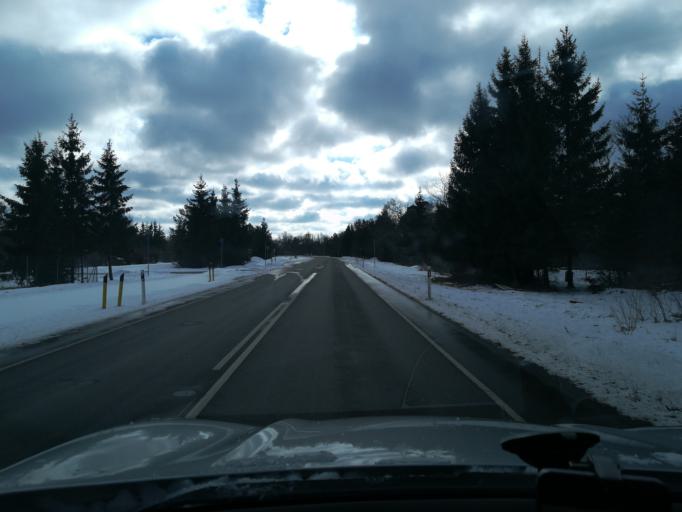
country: EE
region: Harju
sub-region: Paldiski linn
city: Paldiski
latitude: 59.3866
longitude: 24.2379
